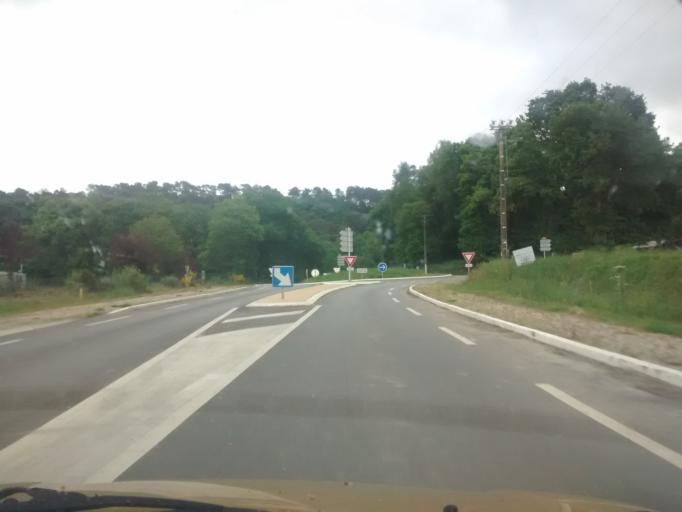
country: FR
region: Brittany
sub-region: Departement du Morbihan
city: Pluherlin
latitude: 47.7072
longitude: -2.3368
